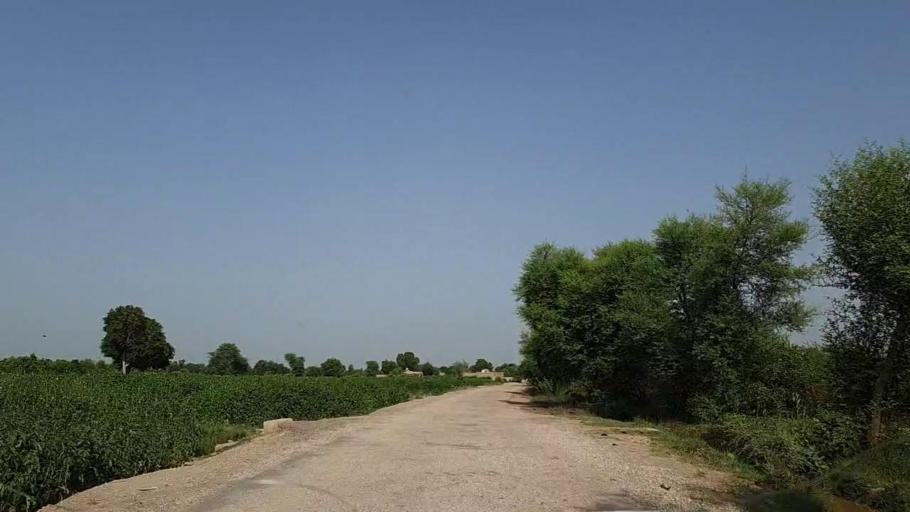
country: PK
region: Sindh
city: Kandiaro
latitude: 27.0717
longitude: 68.1542
